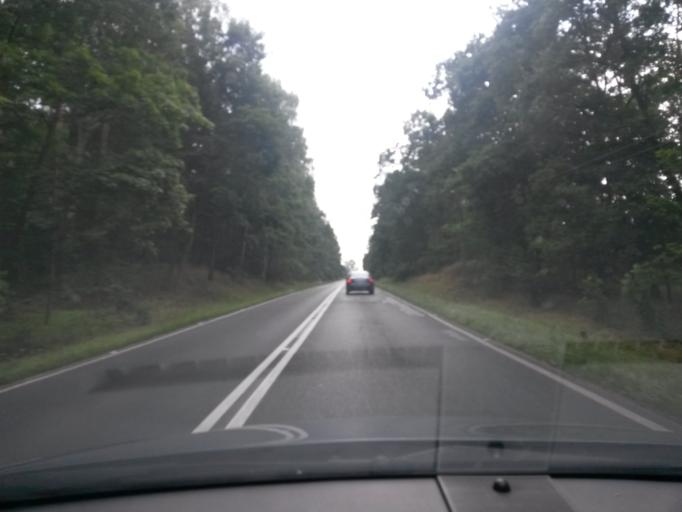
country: PL
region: Greater Poland Voivodeship
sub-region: Powiat poznanski
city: Kornik
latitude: 52.1915
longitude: 17.0594
